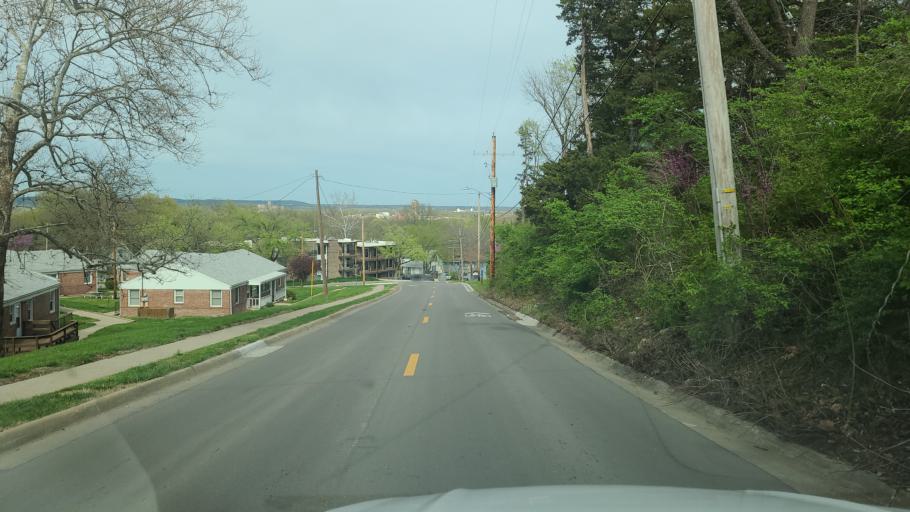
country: US
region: Kansas
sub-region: Douglas County
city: Lawrence
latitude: 38.9636
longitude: -95.2495
